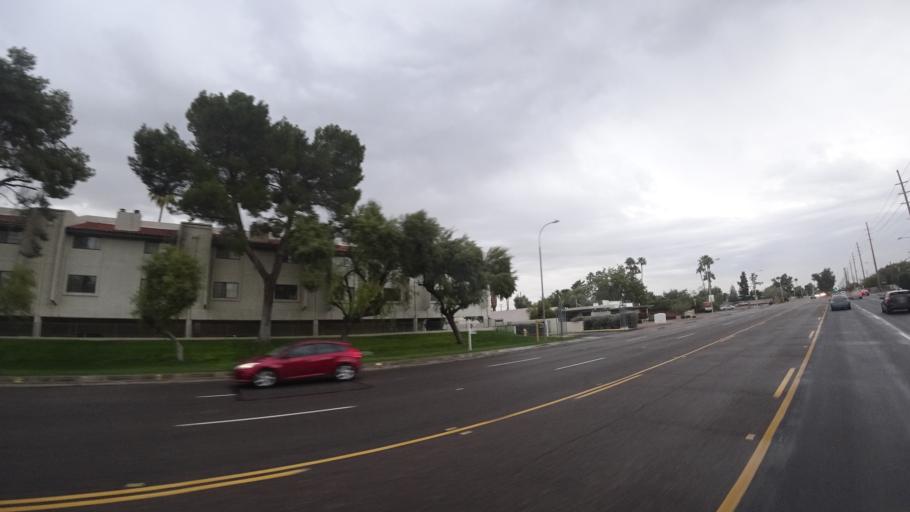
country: US
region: Arizona
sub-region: Maricopa County
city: Scottsdale
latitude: 33.4775
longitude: -111.9090
